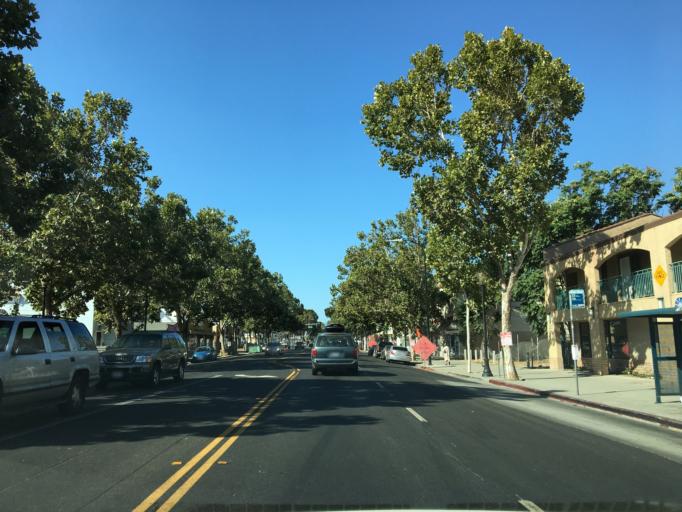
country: US
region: California
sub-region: Santa Clara County
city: San Jose
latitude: 37.3480
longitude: -121.8659
